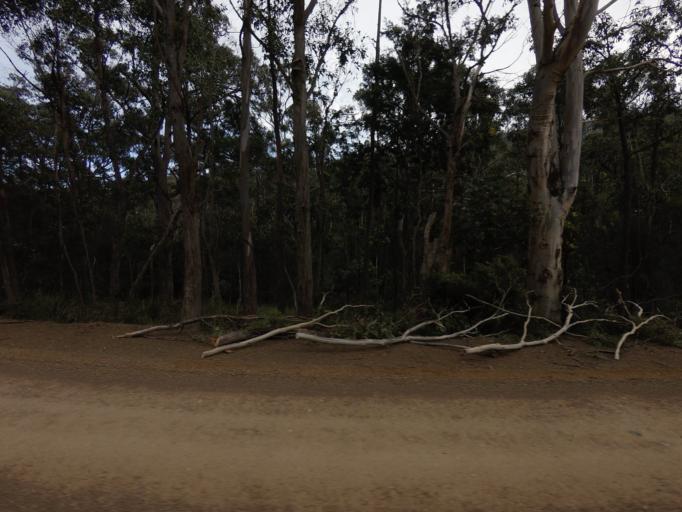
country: AU
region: Tasmania
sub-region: Huon Valley
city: Huonville
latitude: -43.0603
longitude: 147.0947
